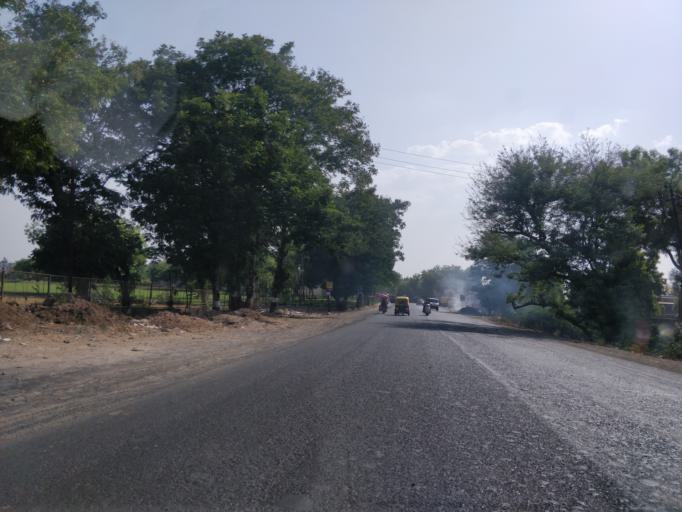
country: IN
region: Gujarat
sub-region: Ahmadabad
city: Naroda
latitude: 23.1013
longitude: 72.7068
